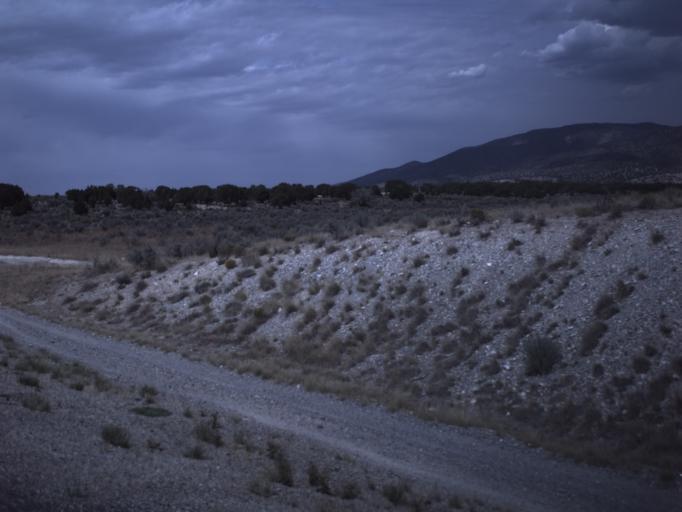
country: US
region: Utah
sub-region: Utah County
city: Eagle Mountain
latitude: 40.2321
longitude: -112.1914
